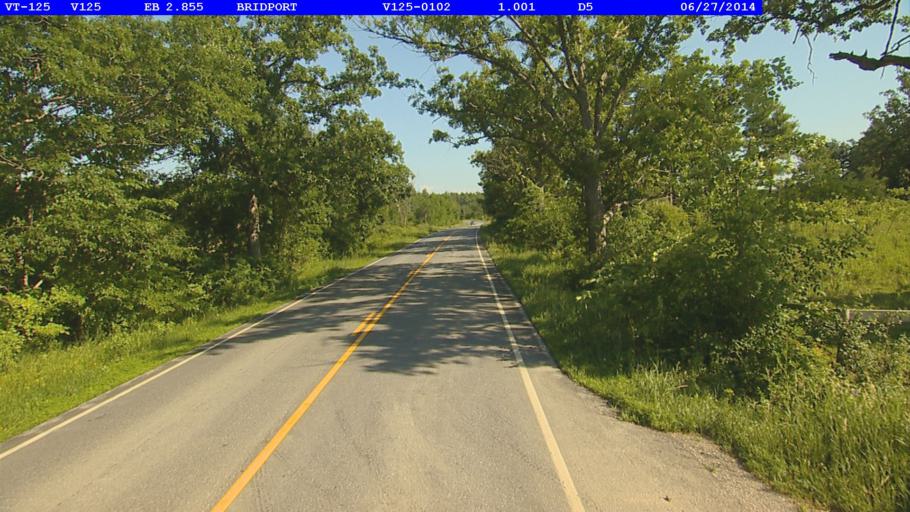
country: US
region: New York
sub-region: Essex County
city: Port Henry
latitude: 44.0081
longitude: -73.3857
